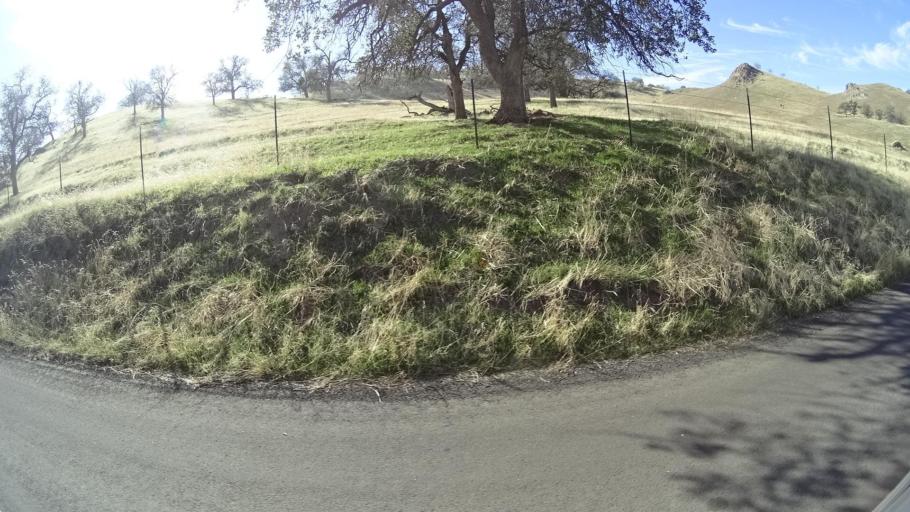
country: US
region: California
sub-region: Kern County
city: Alta Sierra
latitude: 35.6949
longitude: -118.8367
